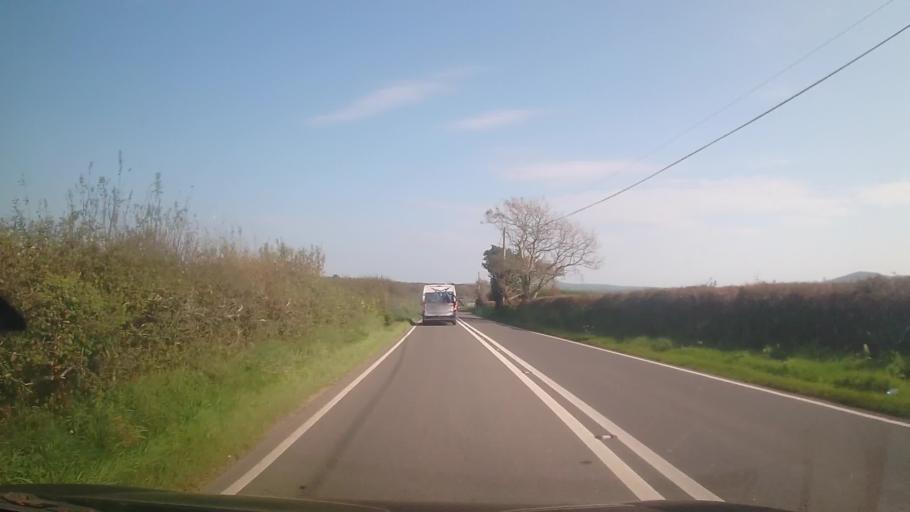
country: GB
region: Wales
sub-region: Pembrokeshire
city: Nevern
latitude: 52.0090
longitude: -4.7262
